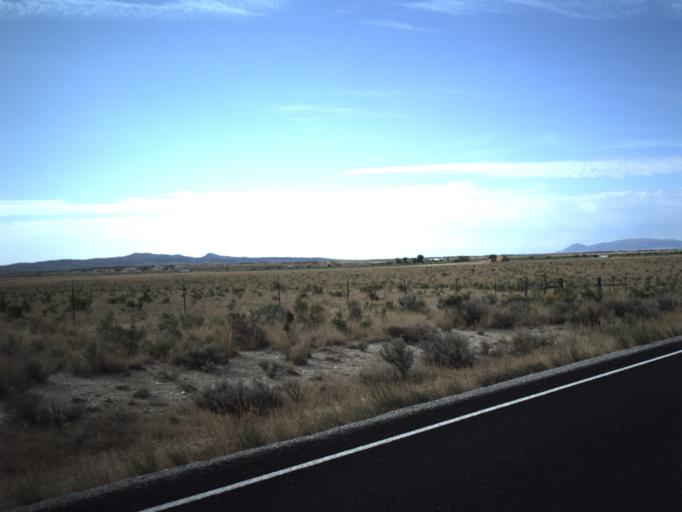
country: US
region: Idaho
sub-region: Cassia County
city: Burley
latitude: 41.7791
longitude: -113.4891
